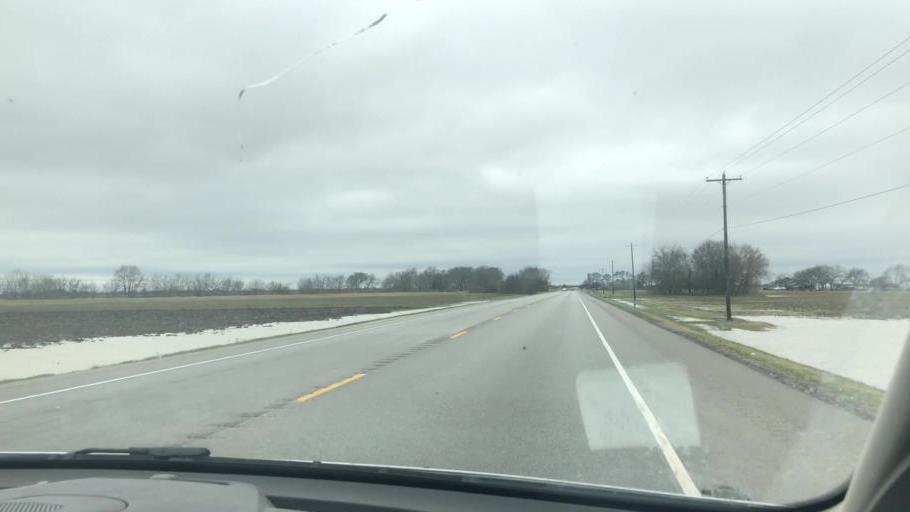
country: US
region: Texas
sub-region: Matagorda County
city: Bay City
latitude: 29.0476
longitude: -95.9715
